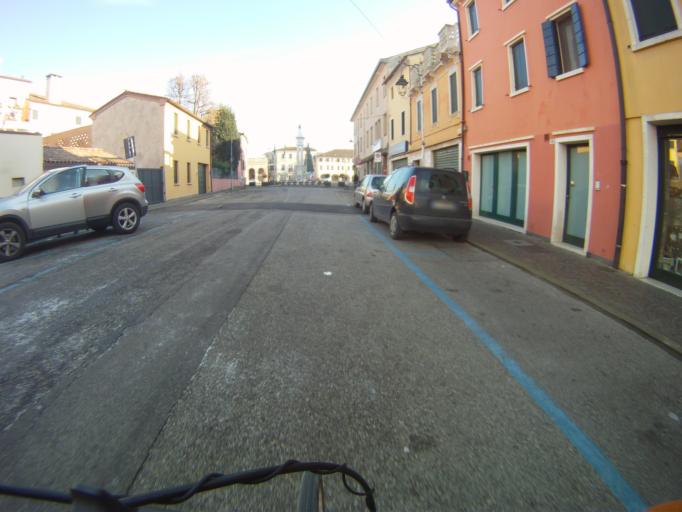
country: IT
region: Veneto
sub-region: Provincia di Padova
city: Piove di Sacco-Piovega
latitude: 45.2973
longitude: 12.0336
